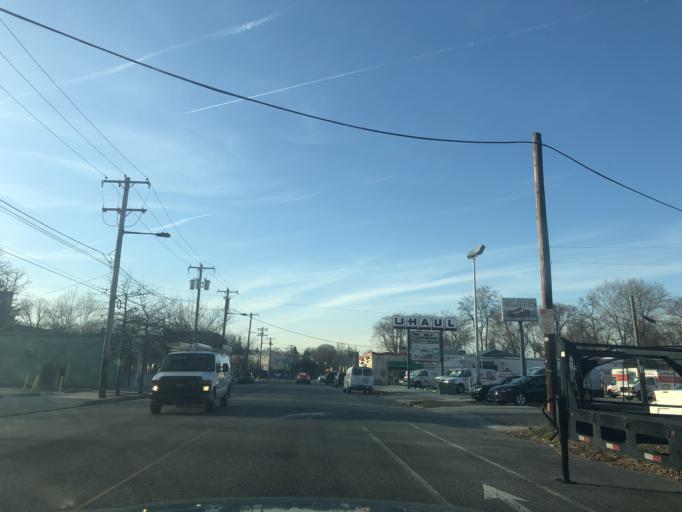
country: US
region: Pennsylvania
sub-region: Delaware County
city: Millbourne
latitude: 39.9836
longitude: -75.2437
